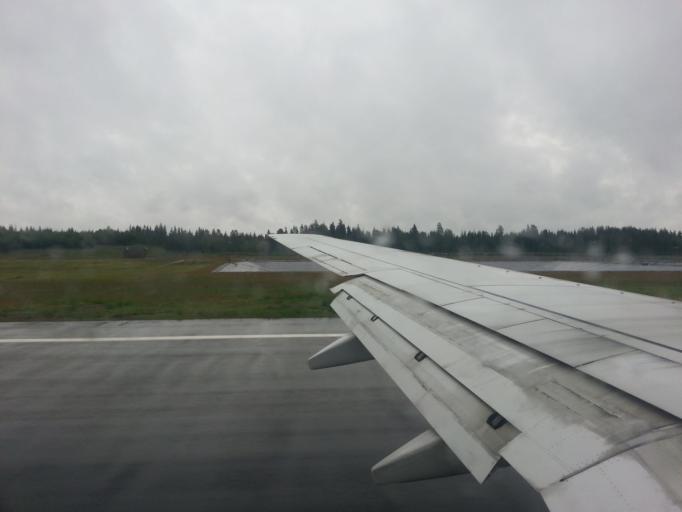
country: NO
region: Akershus
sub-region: Ullensaker
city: Jessheim
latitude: 60.1818
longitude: 11.1113
